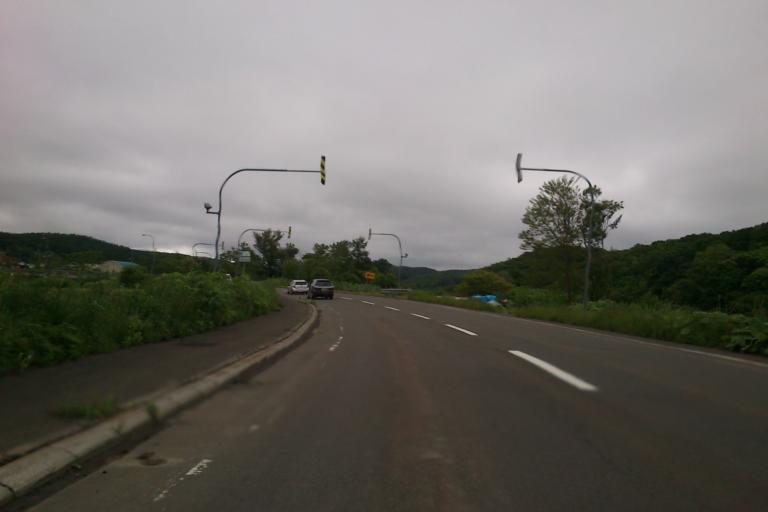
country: JP
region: Hokkaido
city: Ishikari
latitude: 43.3223
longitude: 141.4407
